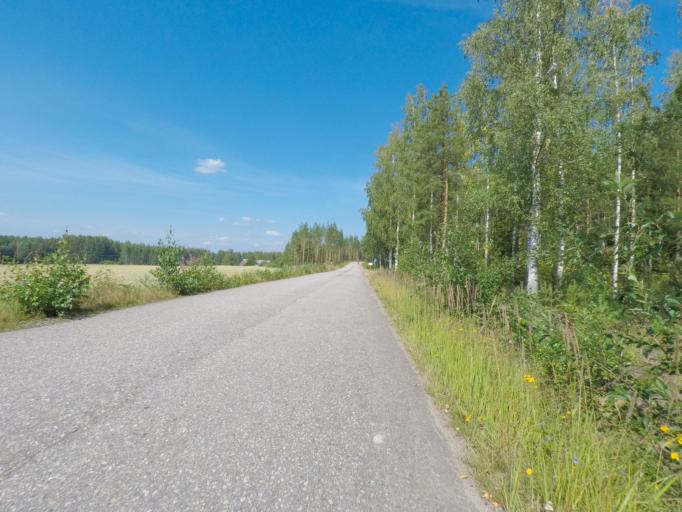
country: FI
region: Southern Savonia
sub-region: Mikkeli
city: Puumala
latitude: 61.4150
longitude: 28.0920
